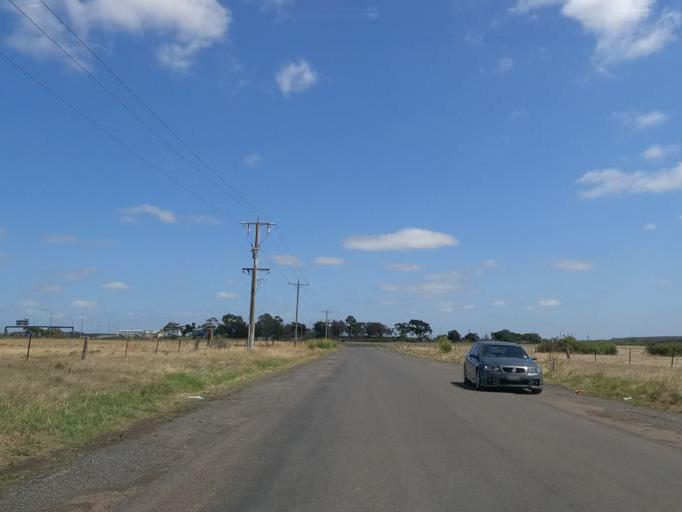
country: AU
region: Victoria
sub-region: Hume
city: Westmeadows
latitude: -37.6786
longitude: 144.8699
